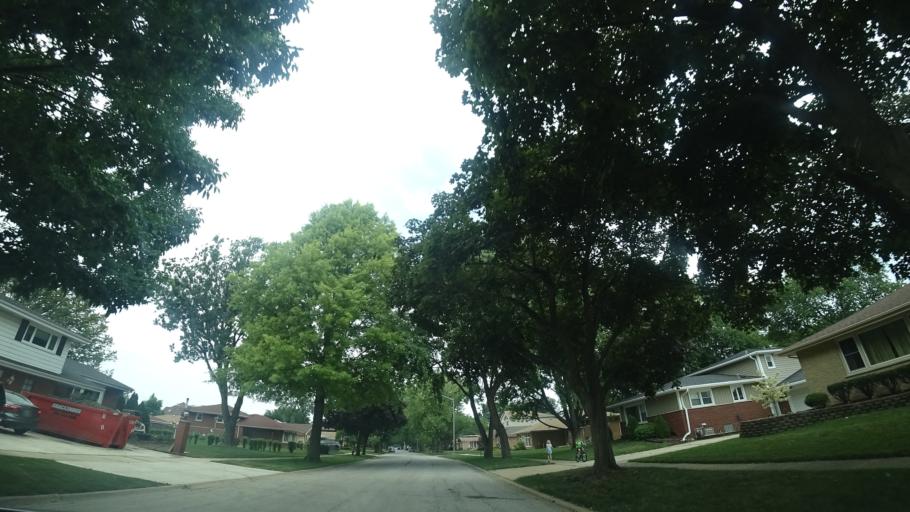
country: US
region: Illinois
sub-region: Cook County
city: Oak Lawn
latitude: 41.6997
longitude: -87.7291
